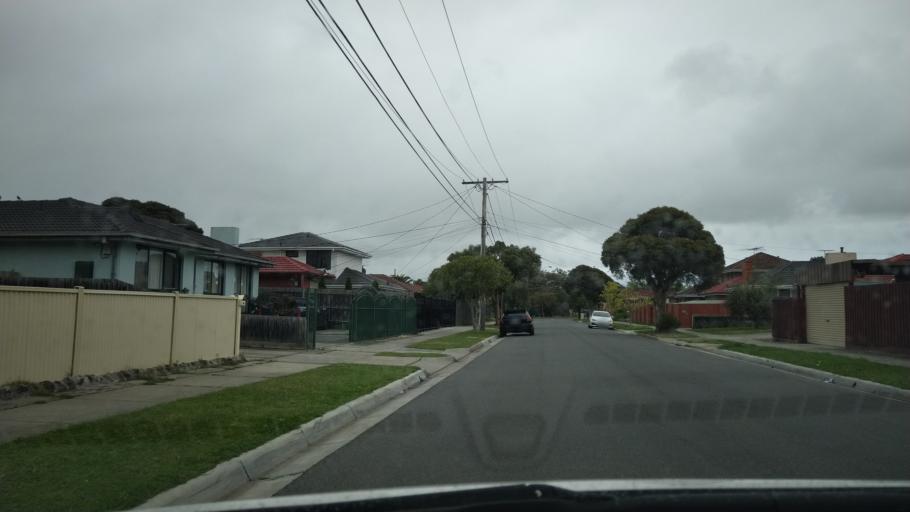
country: AU
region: Victoria
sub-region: Greater Dandenong
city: Keysborough
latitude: -37.9810
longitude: 145.1691
